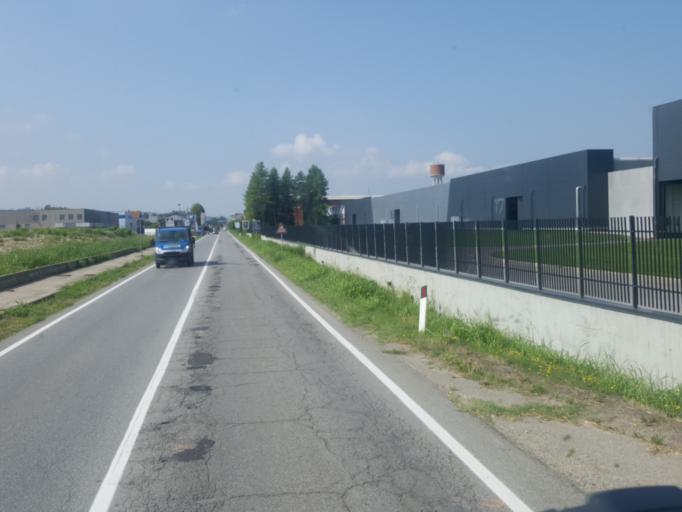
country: IT
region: Piedmont
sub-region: Provincia di Cuneo
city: Mussotto
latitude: 44.7171
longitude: 8.0337
